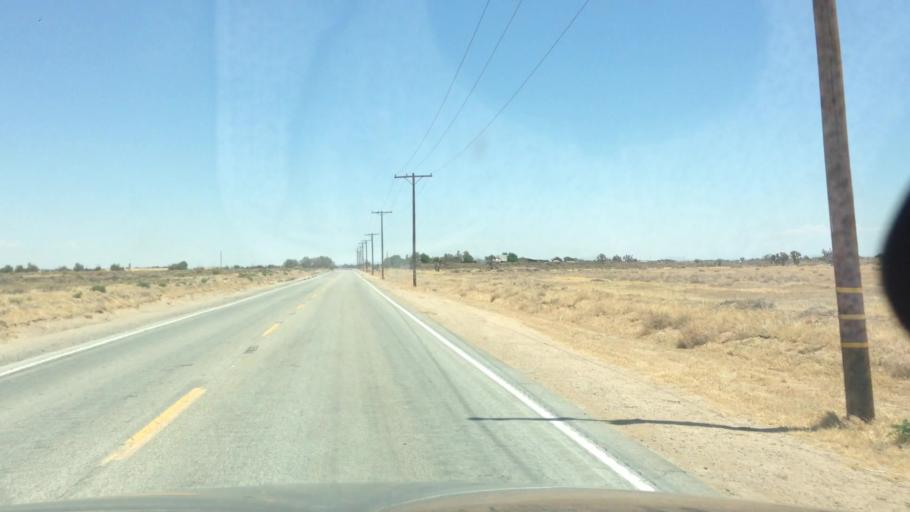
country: US
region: California
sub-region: Los Angeles County
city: Leona Valley
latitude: 34.7763
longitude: -118.3146
